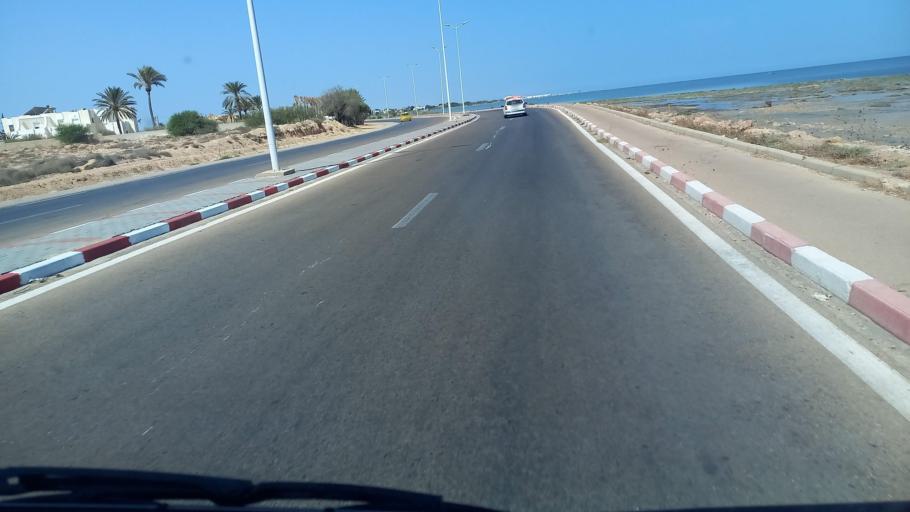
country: TN
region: Madanin
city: Houmt Souk
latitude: 33.8744
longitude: 10.9051
